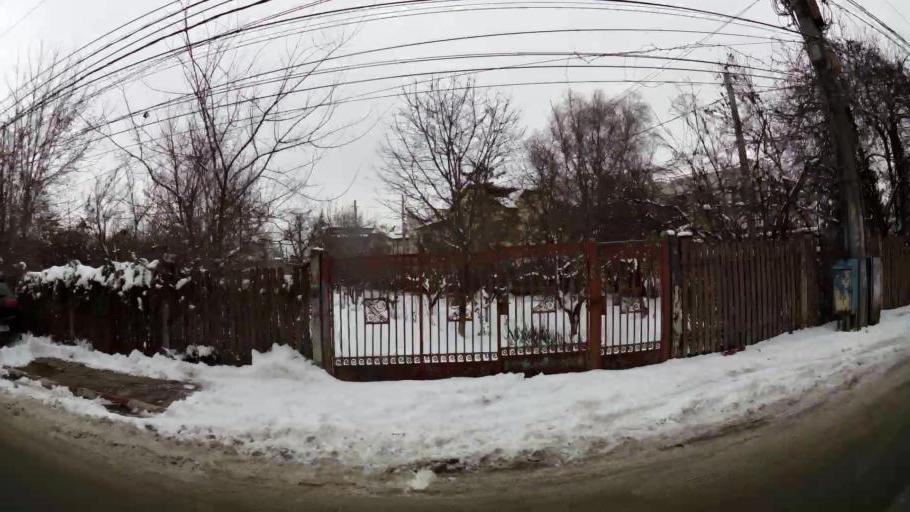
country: RO
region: Ilfov
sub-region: Comuna Tunari
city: Tunari
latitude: 44.5115
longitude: 26.1089
